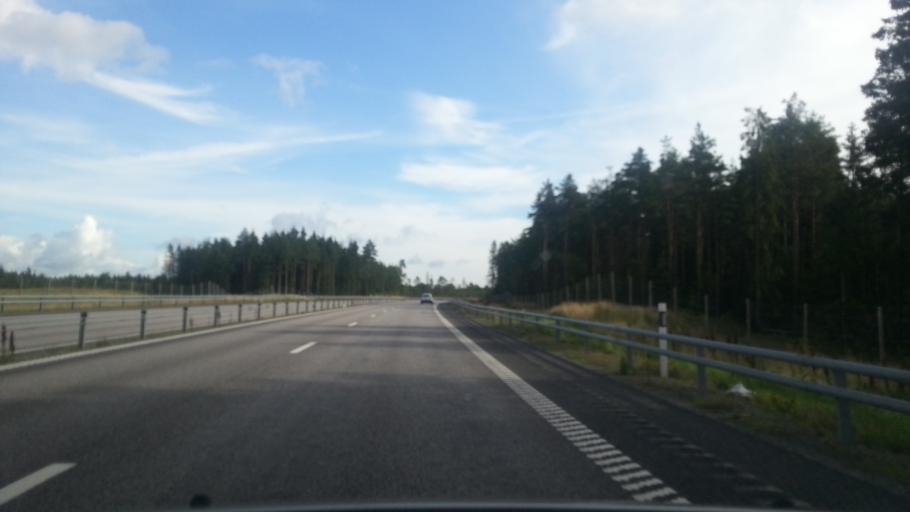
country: SE
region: Vaestra Goetaland
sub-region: Trollhattan
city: Sjuntorp
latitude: 58.2293
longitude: 12.2195
